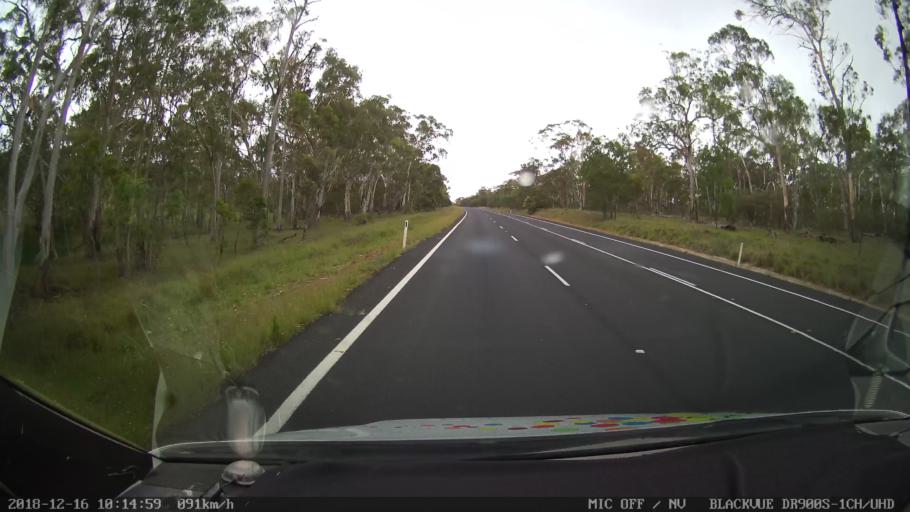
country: AU
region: New South Wales
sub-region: Tenterfield Municipality
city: Carrolls Creek
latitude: -29.2814
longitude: 151.9683
